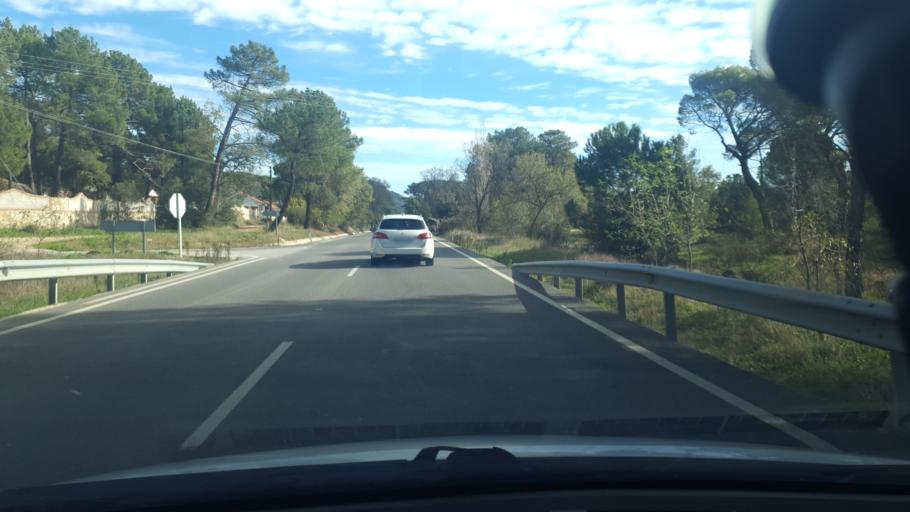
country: ES
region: Castille and Leon
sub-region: Provincia de Avila
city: La Adrada
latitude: 40.3112
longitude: -4.6588
